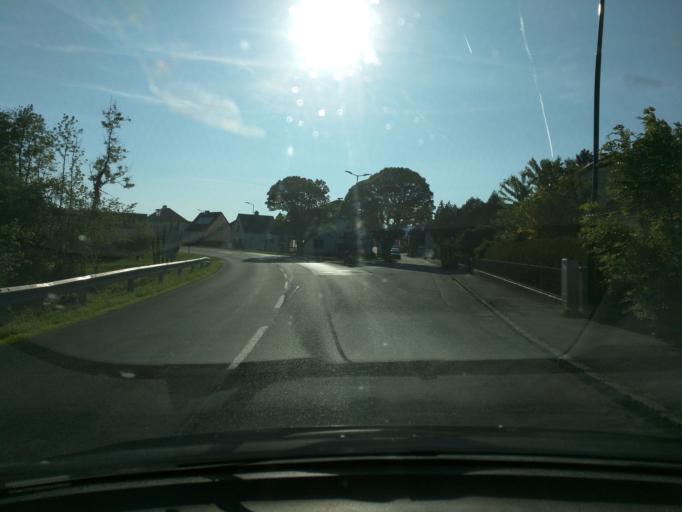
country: AT
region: Lower Austria
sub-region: Politischer Bezirk Melk
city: Neumarkt an der Ybbs
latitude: 48.1415
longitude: 15.0565
